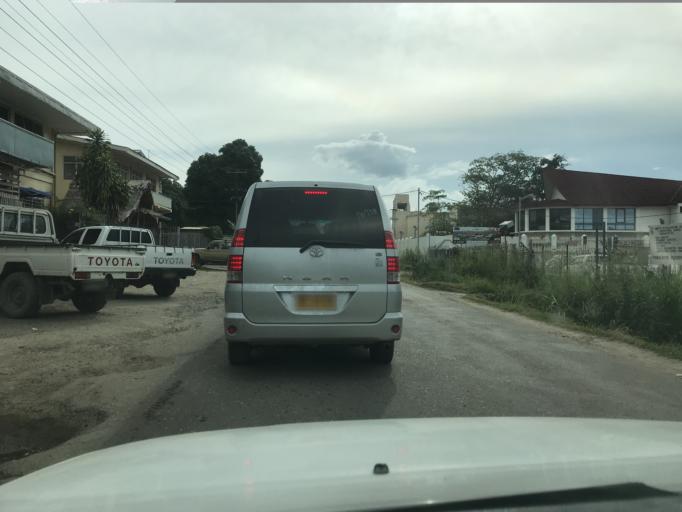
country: SB
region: Guadalcanal
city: Honiara
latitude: -9.4317
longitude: 159.9506
